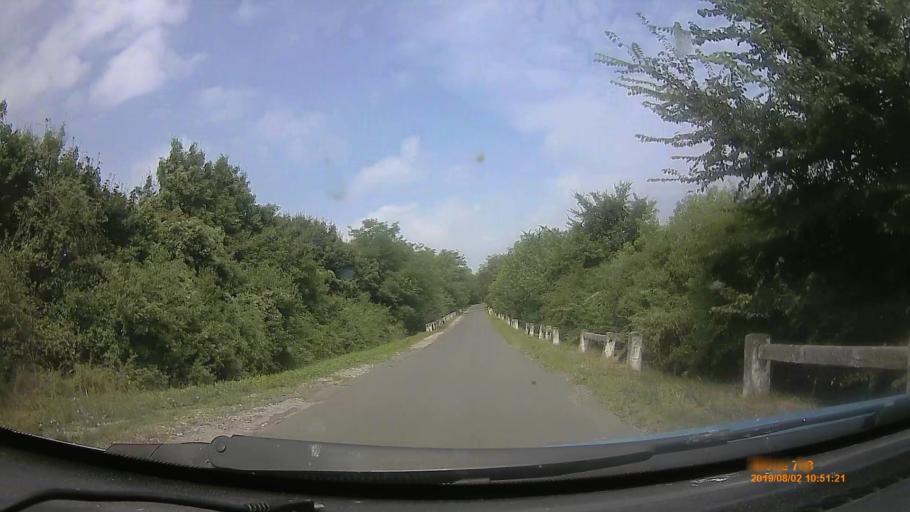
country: HU
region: Baranya
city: Buekkoesd
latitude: 46.0854
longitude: 17.9690
